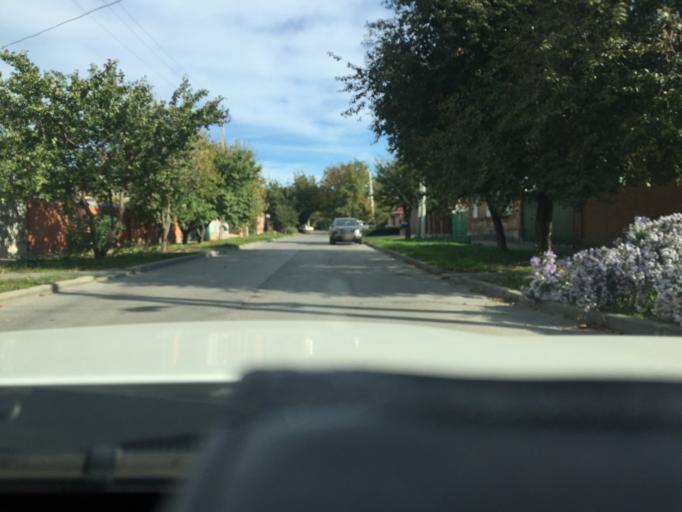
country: RU
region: Rostov
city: Imeni Chkalova
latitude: 47.2716
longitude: 39.7940
